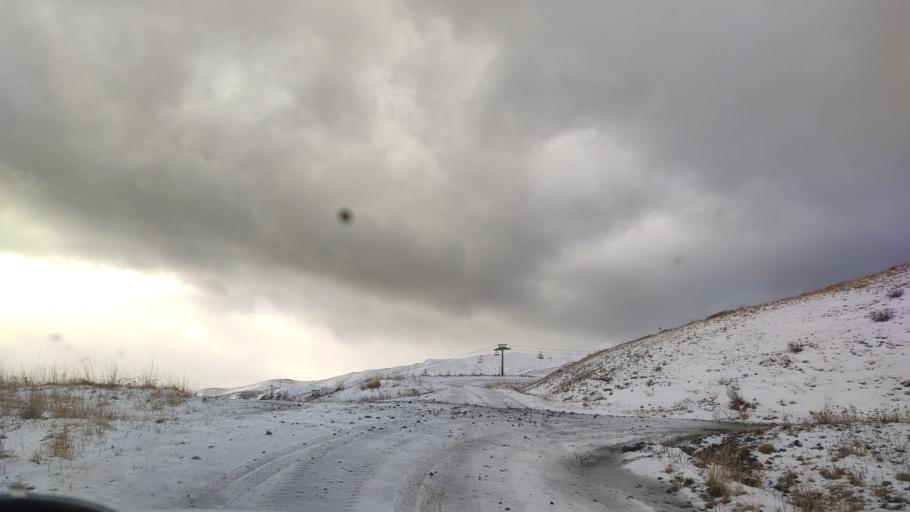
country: FR
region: Rhone-Alpes
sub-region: Departement de la Savoie
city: Saint-Etienne-de-Cuines
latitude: 45.2544
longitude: 6.2303
